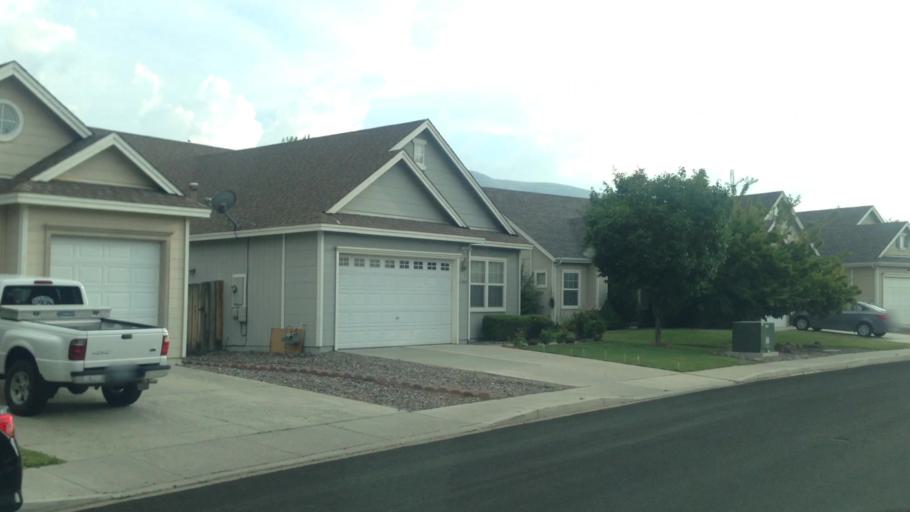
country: US
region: Nevada
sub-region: Washoe County
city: Lemmon Valley
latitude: 39.6328
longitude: -119.8747
